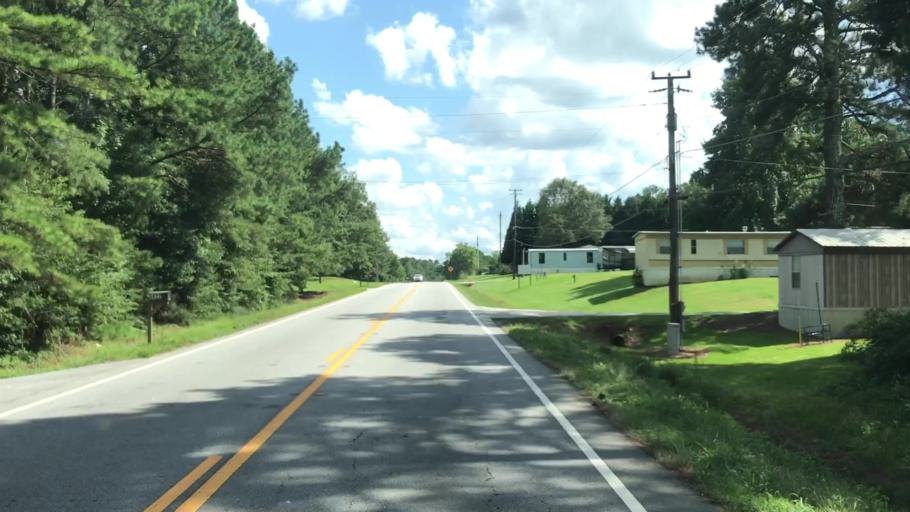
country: US
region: Georgia
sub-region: Newton County
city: Oxford
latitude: 33.6787
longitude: -83.8505
